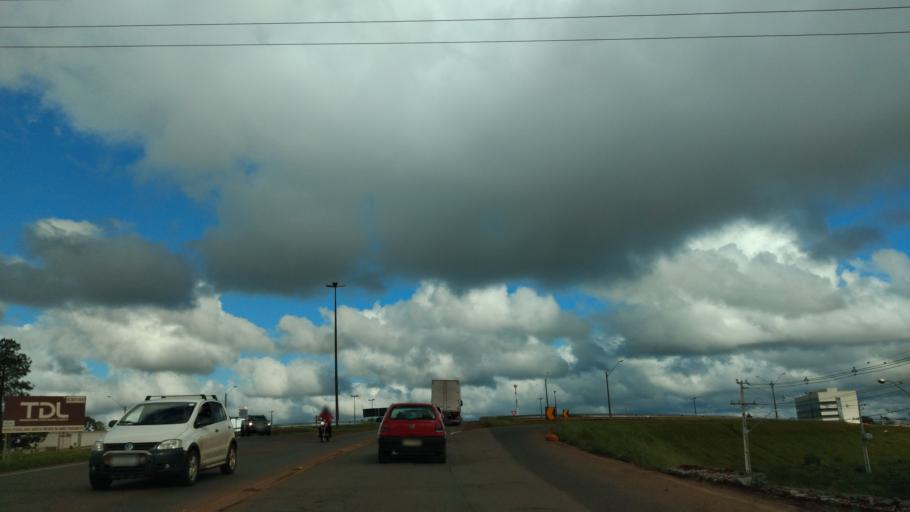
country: BR
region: Parana
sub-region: Guarapuava
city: Guarapuava
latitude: -25.3626
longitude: -51.4769
